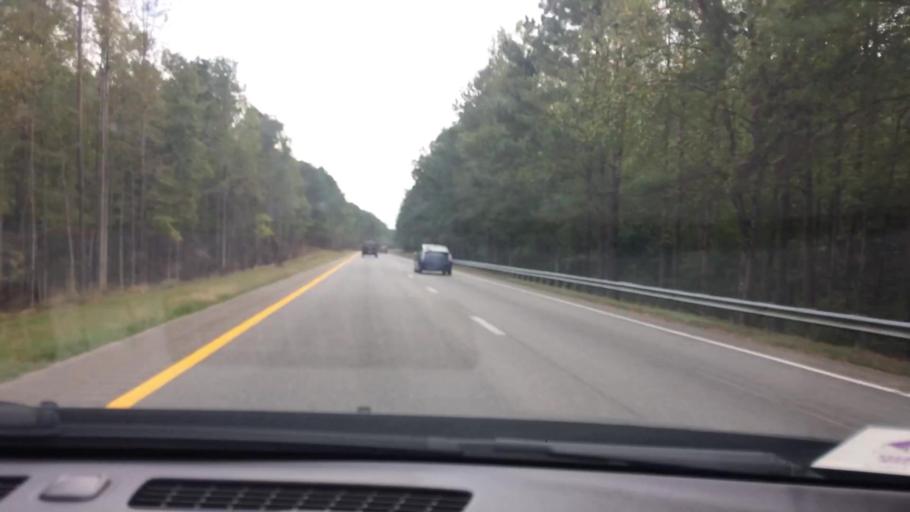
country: US
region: North Carolina
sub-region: Wake County
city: Zebulon
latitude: 35.7939
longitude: -78.1613
